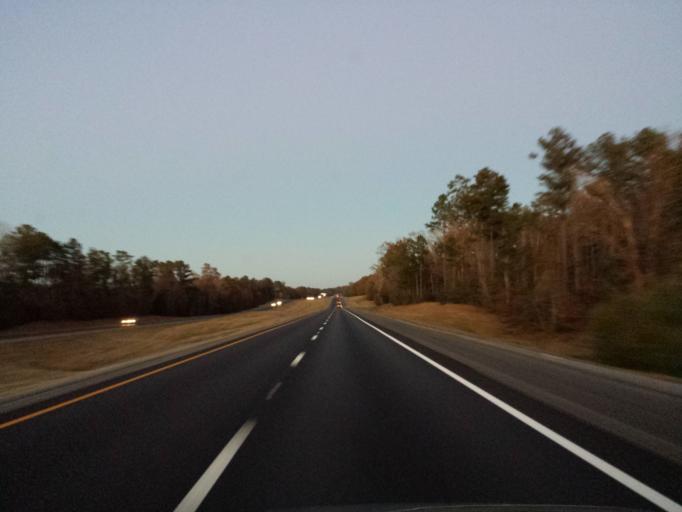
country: US
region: Mississippi
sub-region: Jones County
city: Sharon
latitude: 31.7447
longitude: -89.0814
